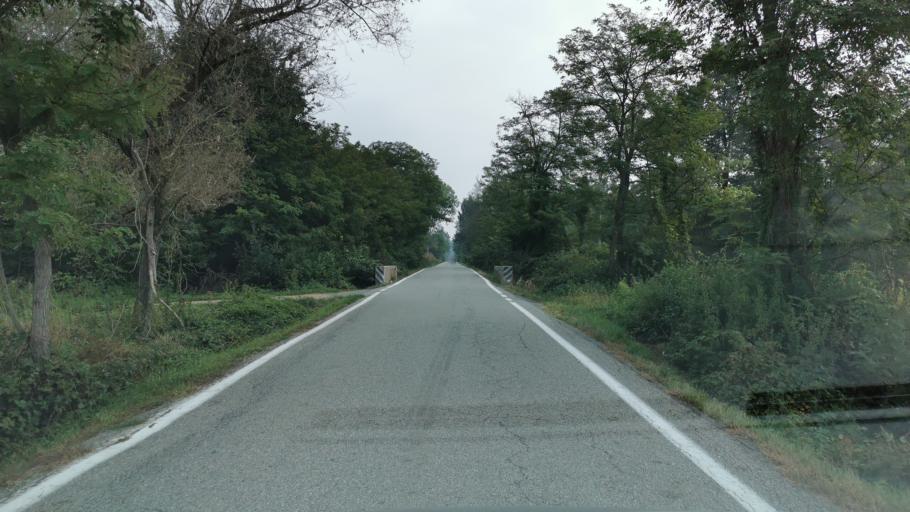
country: IT
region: Piedmont
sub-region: Provincia di Torino
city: Foglizzo
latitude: 45.2489
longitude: 7.8261
